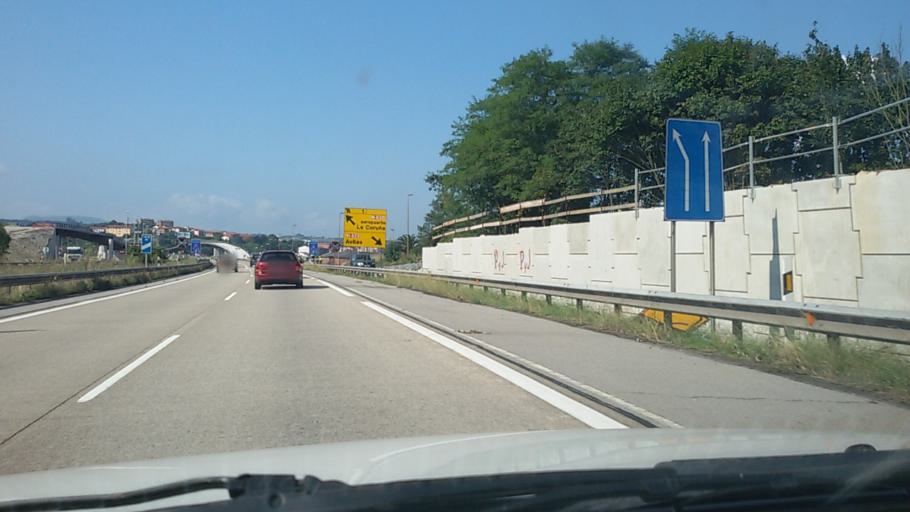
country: ES
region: Asturias
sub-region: Province of Asturias
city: Aviles
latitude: 43.5534
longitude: -5.8929
